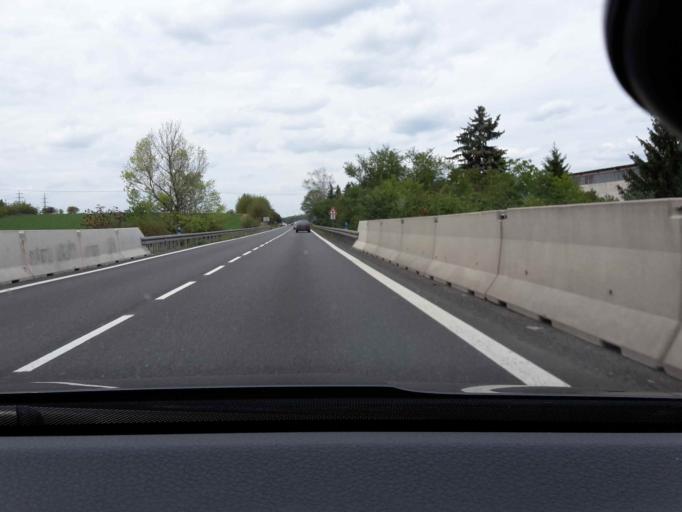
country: CZ
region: Central Bohemia
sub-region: Okres Benesov
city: Benesov
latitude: 49.7901
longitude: 14.6783
